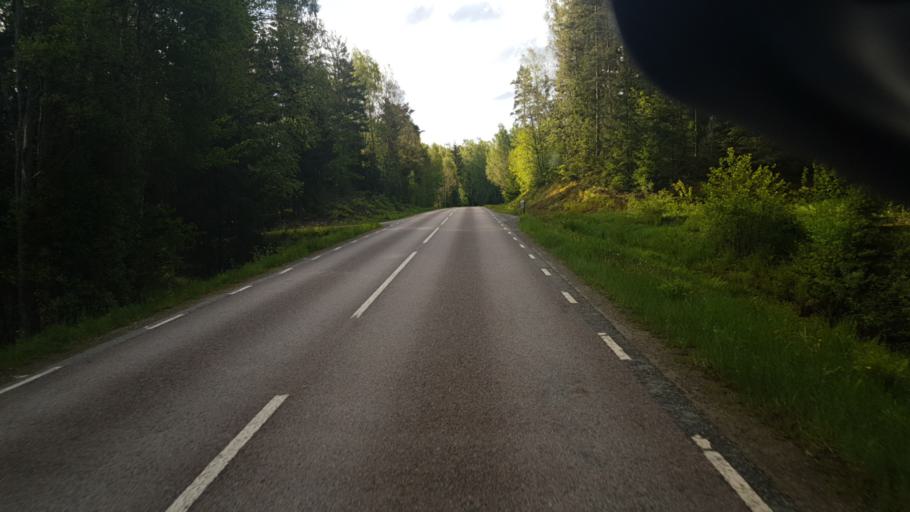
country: SE
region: Vaermland
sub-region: Arvika Kommun
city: Arvika
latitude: 59.5870
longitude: 12.5480
